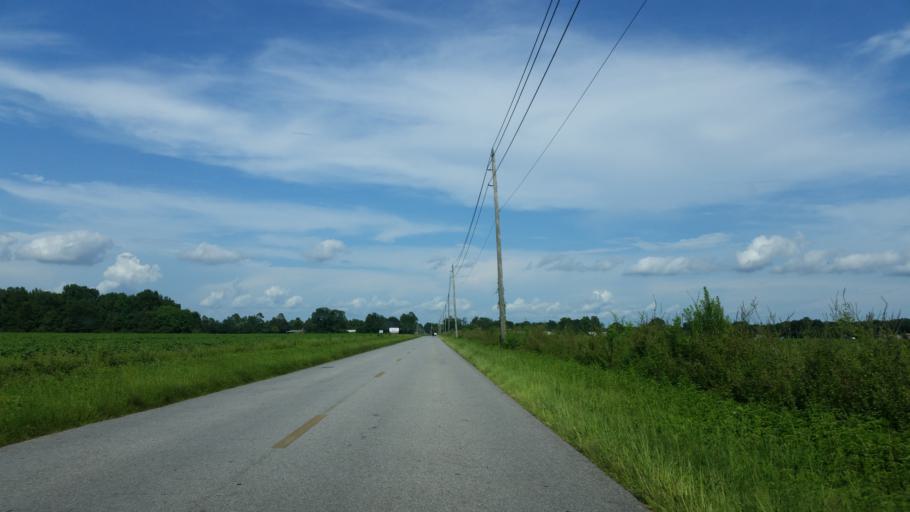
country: US
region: Florida
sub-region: Santa Rosa County
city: Pace
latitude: 30.6185
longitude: -87.1556
